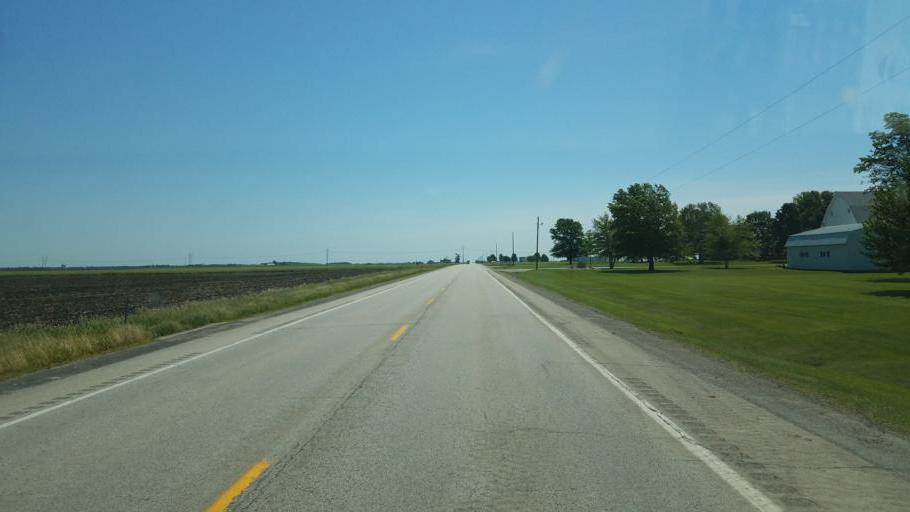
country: US
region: Illinois
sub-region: McLean County
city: Downs
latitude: 40.3120
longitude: -88.8454
